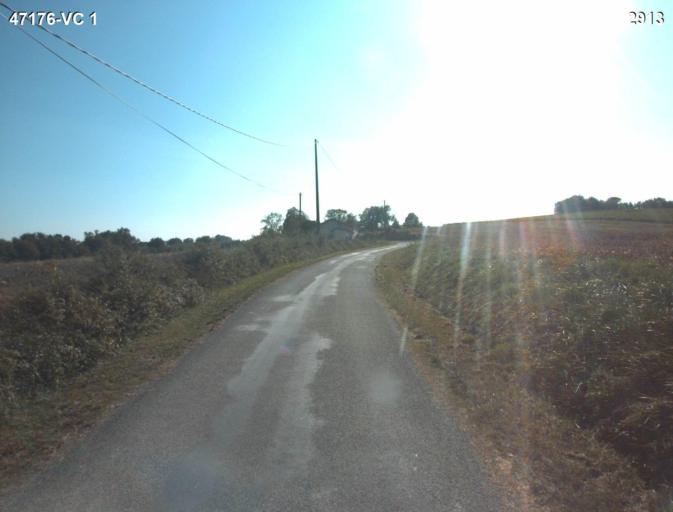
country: FR
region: Aquitaine
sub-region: Departement du Lot-et-Garonne
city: Vianne
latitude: 44.2169
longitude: 0.3018
